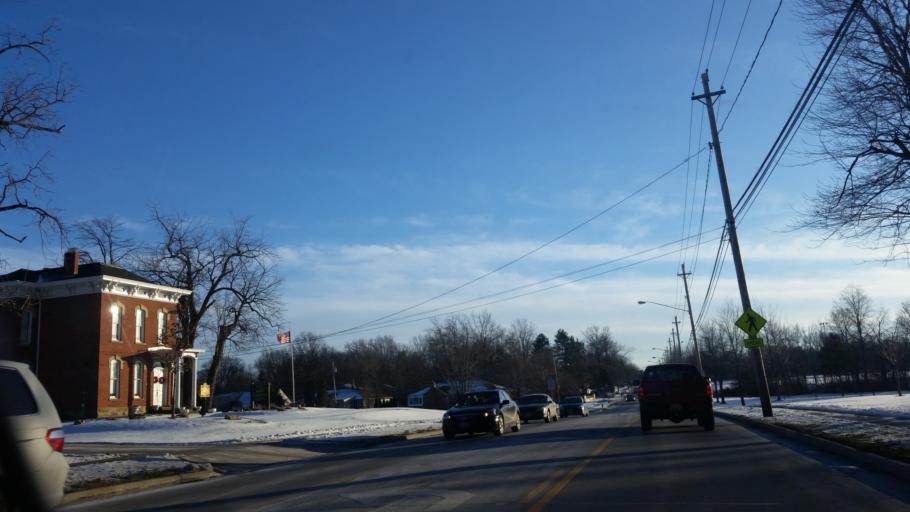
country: US
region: Ohio
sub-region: Cuyahoga County
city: Fairview Park
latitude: 41.4672
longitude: -81.8826
